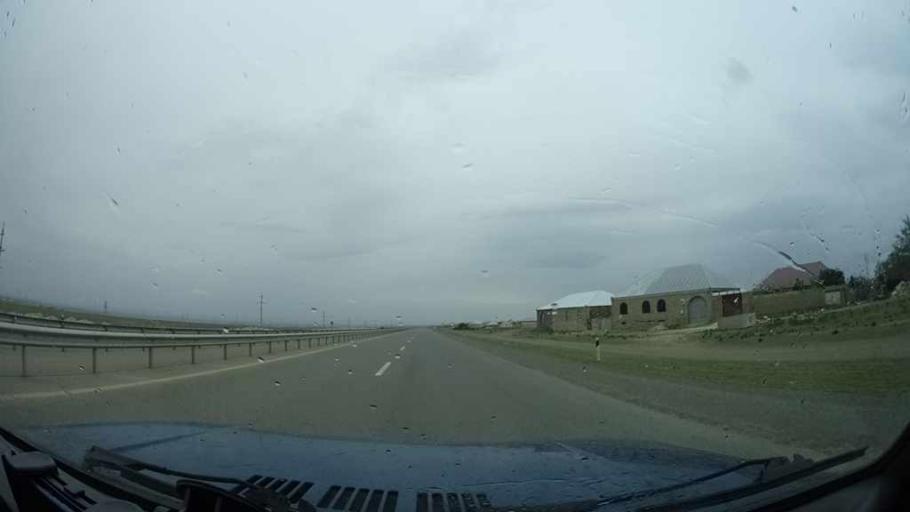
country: AZ
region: Ganja City
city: Ganja
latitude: 40.6373
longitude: 46.4096
